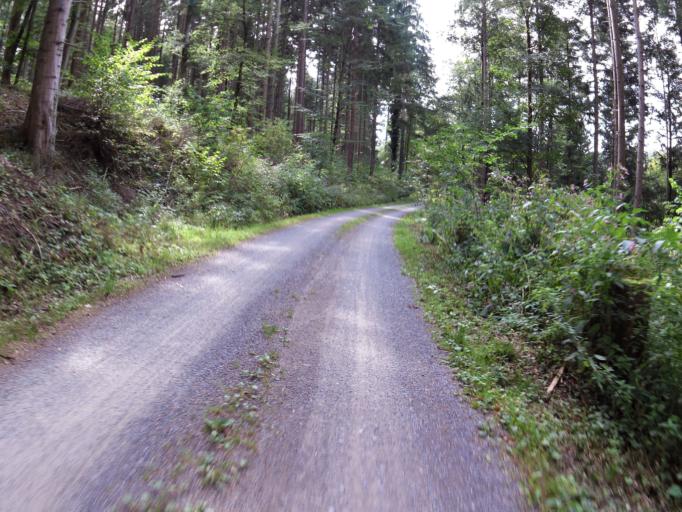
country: DE
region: Baden-Wuerttemberg
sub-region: Freiburg Region
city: Sulz am Neckar
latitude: 48.3525
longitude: 8.6044
